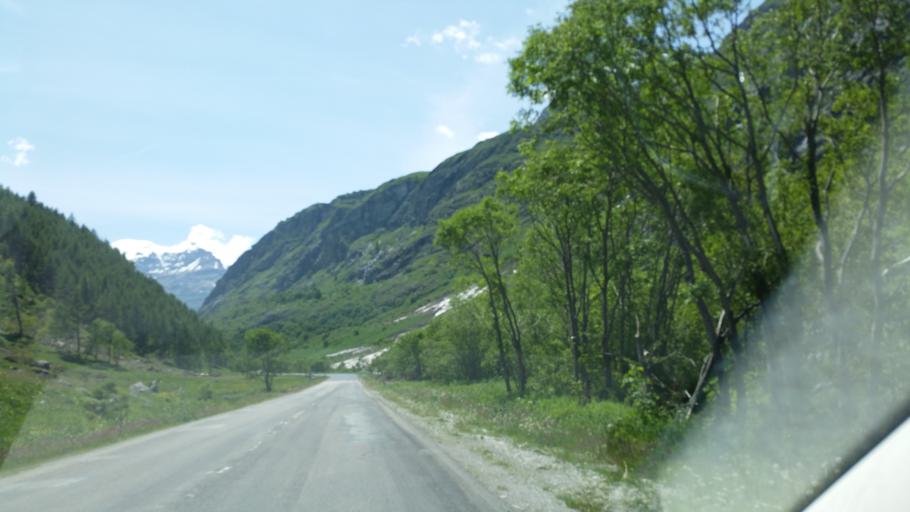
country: FR
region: Rhone-Alpes
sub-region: Departement de la Savoie
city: Val-d'Isere
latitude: 45.3614
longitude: 7.0336
